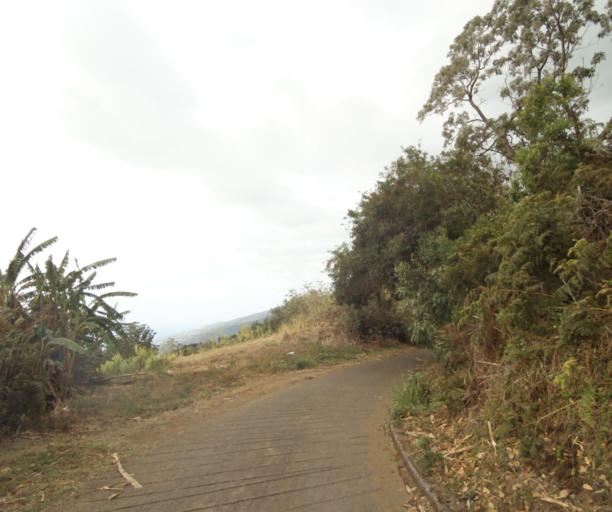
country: RE
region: Reunion
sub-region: Reunion
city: Saint-Paul
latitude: -21.0220
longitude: 55.3235
